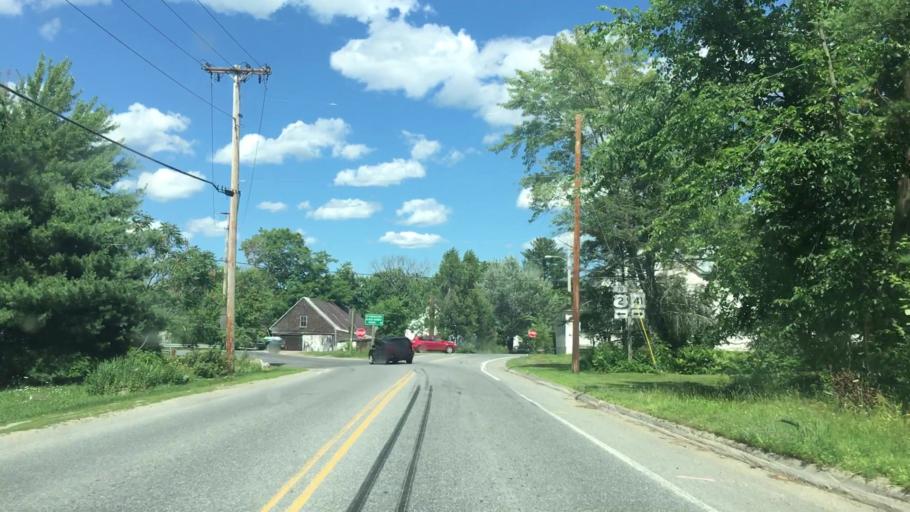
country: US
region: Maine
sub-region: Franklin County
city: New Sharon
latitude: 44.6191
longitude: -70.0753
